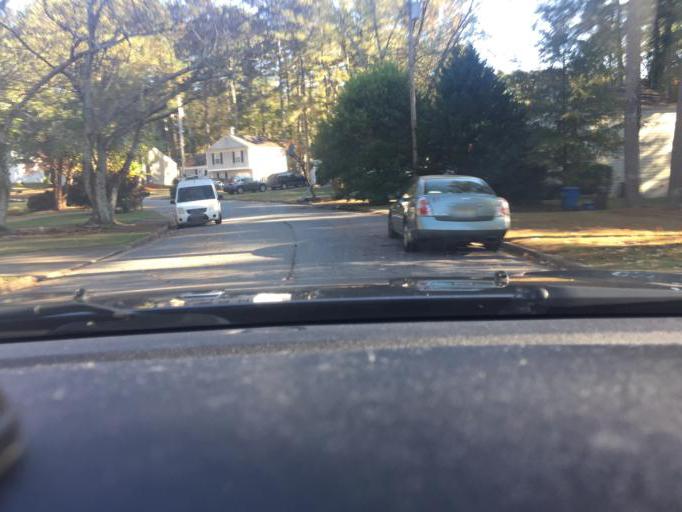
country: US
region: Georgia
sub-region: Fulton County
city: Alpharetta
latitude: 34.0303
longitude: -84.2694
